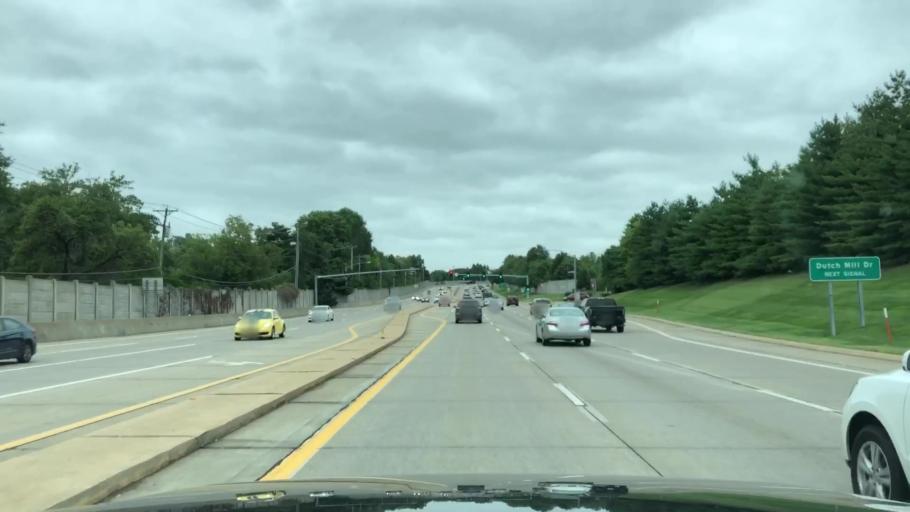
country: US
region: Missouri
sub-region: Saint Louis County
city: Manchester
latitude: 38.6100
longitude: -90.5114
